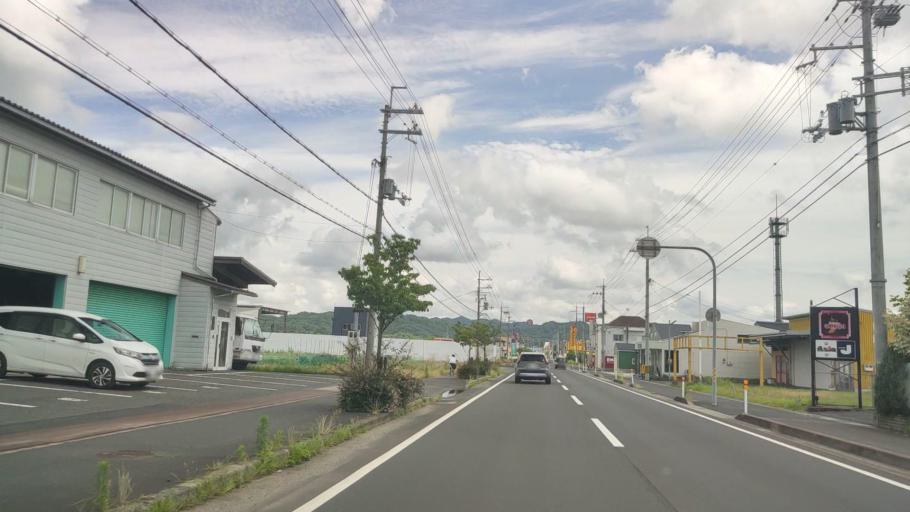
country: JP
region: Kyoto
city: Miyazu
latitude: 35.5977
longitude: 135.0889
